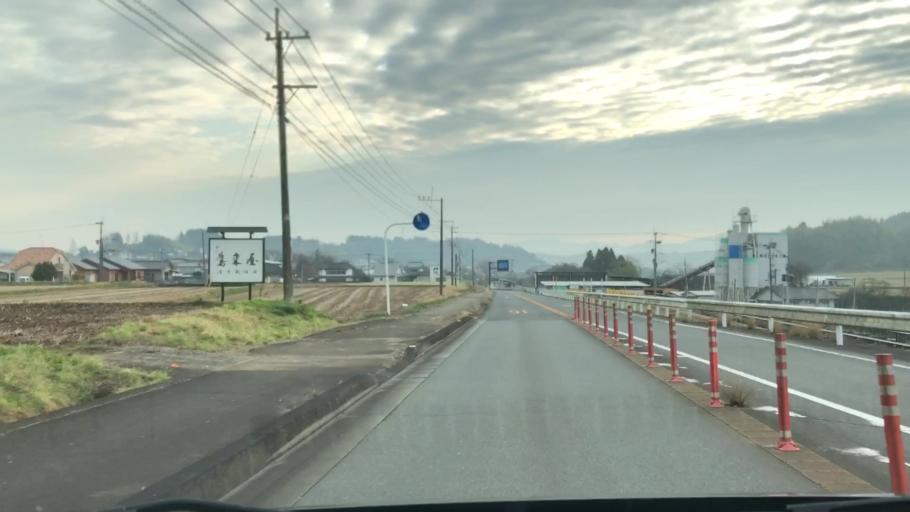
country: JP
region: Oita
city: Takedamachi
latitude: 32.9696
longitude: 131.4654
